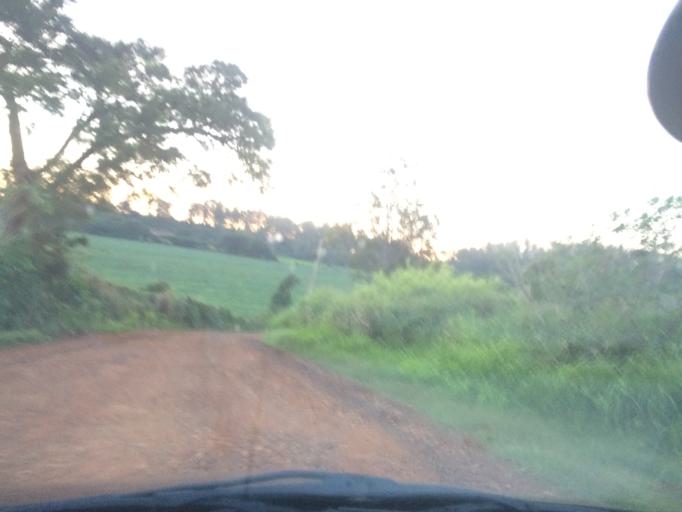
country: BR
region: Sao Paulo
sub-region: Tambau
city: Tambau
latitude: -21.7049
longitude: -47.2064
